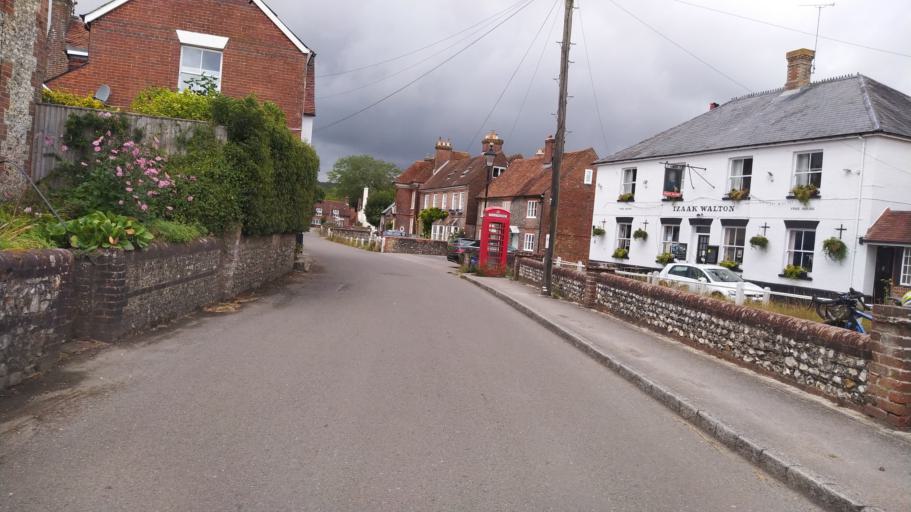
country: GB
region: England
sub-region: Hampshire
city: Petersfield
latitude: 50.9943
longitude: -1.0302
